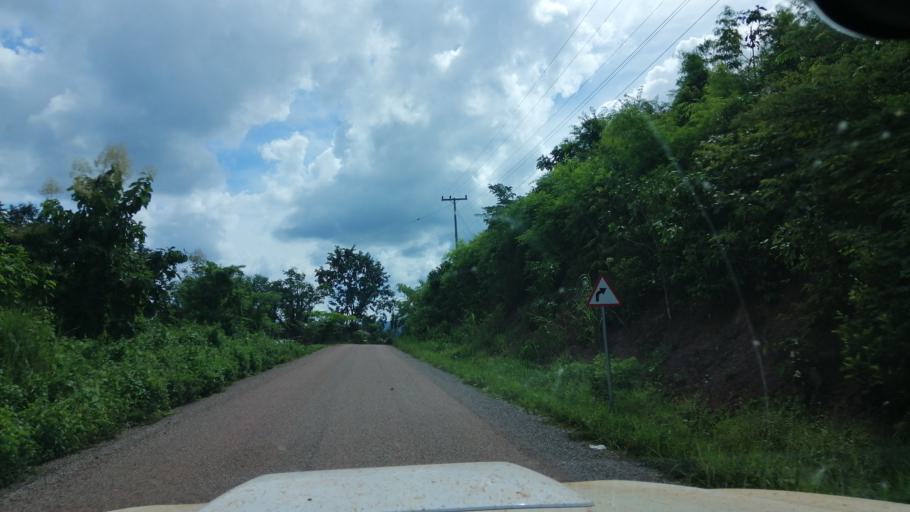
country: TH
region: Uttaradit
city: Ban Khok
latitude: 18.3660
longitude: 101.1430
